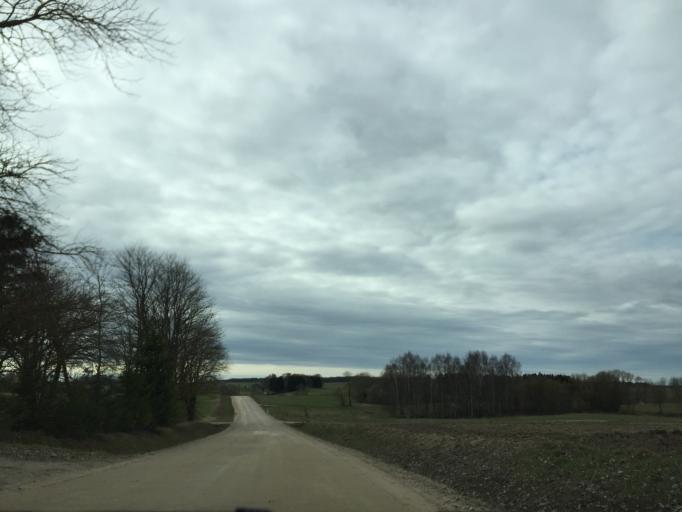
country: LT
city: Silale
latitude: 55.6187
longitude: 22.1995
